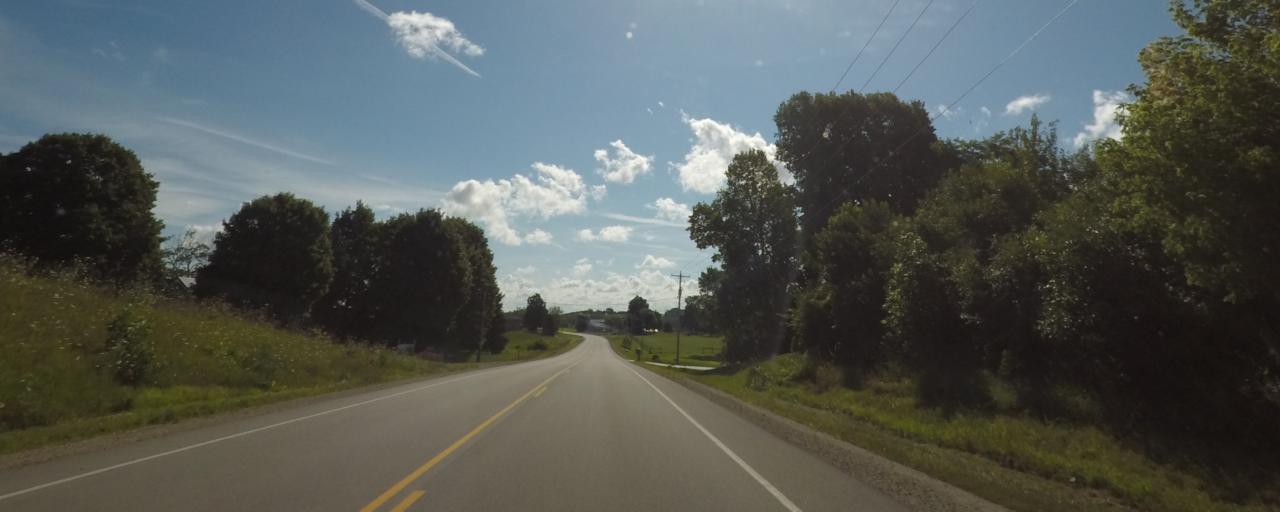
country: US
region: Wisconsin
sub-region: Jefferson County
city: Ixonia
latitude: 43.0678
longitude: -88.6171
